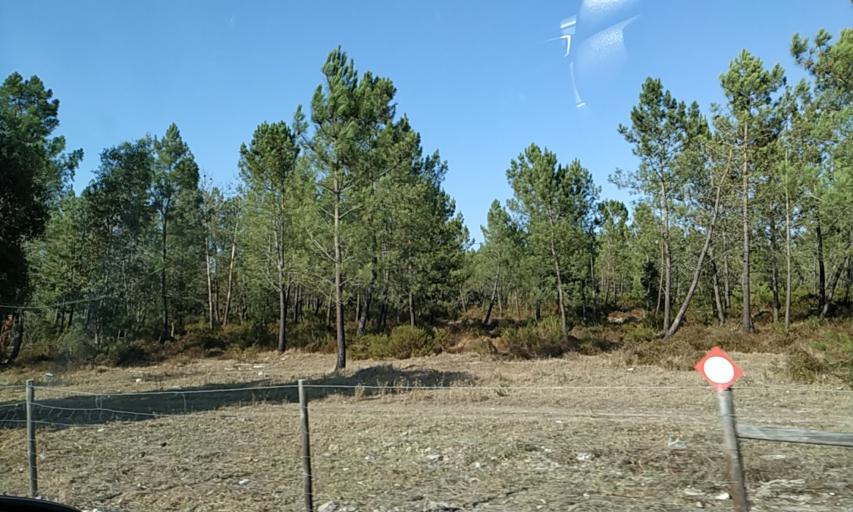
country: PT
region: Santarem
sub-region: Almeirim
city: Fazendas de Almeirim
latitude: 39.1260
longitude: -8.6037
